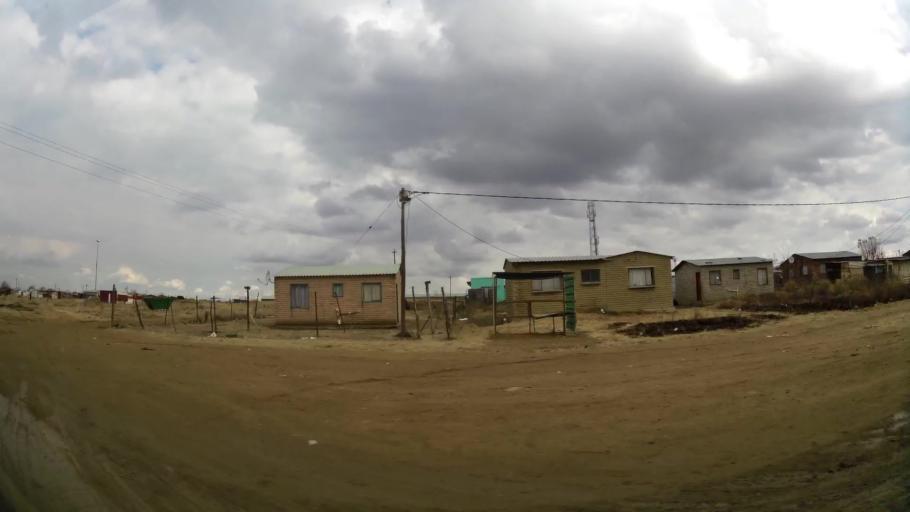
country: ZA
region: Orange Free State
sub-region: Fezile Dabi District Municipality
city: Sasolburg
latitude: -26.8779
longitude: 27.8754
